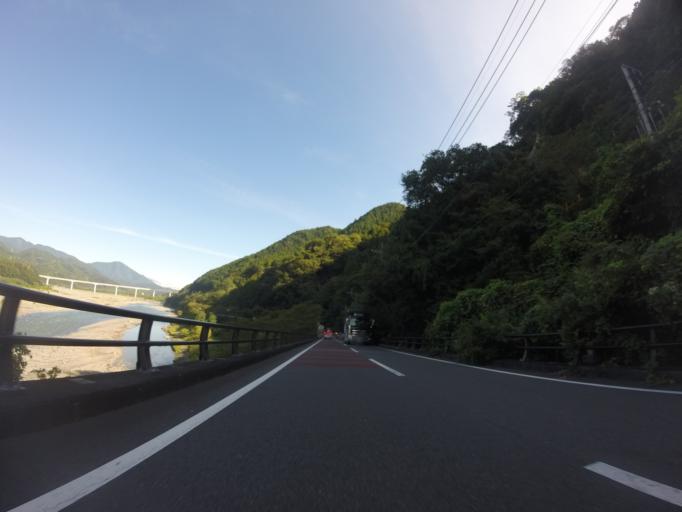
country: JP
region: Shizuoka
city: Fujinomiya
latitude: 35.3002
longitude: 138.4565
